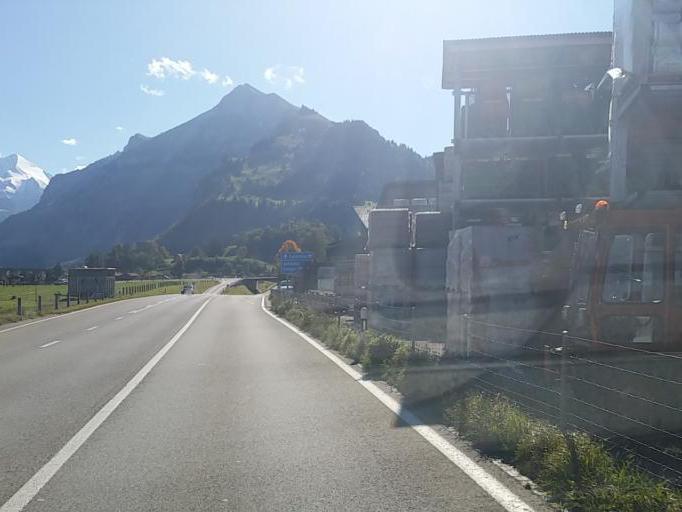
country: CH
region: Bern
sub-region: Frutigen-Niedersimmental District
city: Frutigen
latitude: 46.5865
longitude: 7.6526
